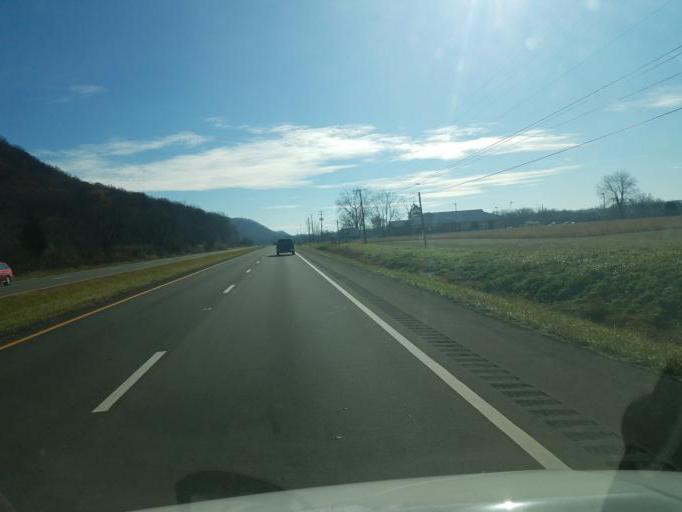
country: US
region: Ohio
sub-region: Scioto County
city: Lucasville
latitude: 38.8390
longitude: -82.9844
